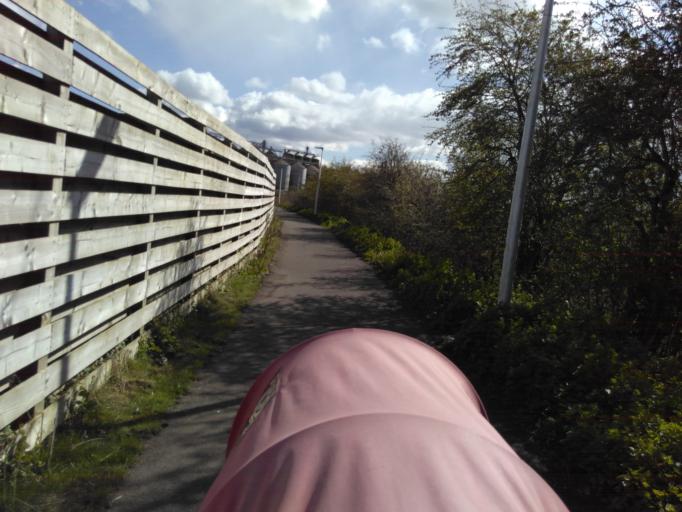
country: GB
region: Scotland
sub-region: Midlothian
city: Loanhead
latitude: 55.8879
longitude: -3.1475
